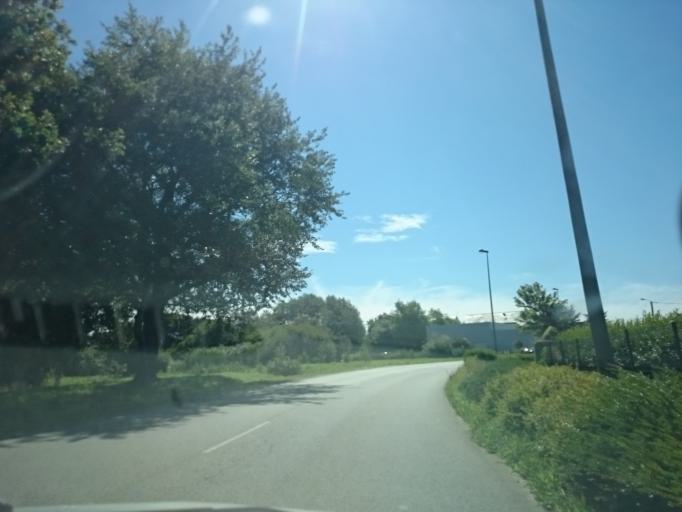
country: FR
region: Brittany
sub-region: Departement du Finistere
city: Saint-Renan
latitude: 48.4364
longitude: -4.6227
